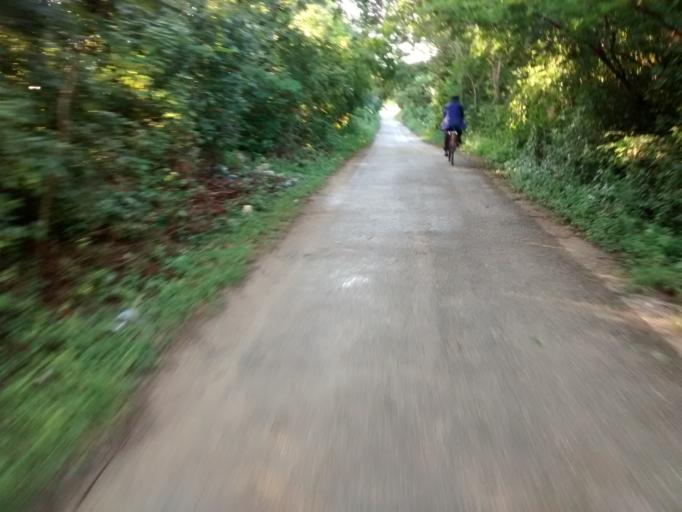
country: MX
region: Yucatan
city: Valladolid
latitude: 20.7248
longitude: -88.2289
